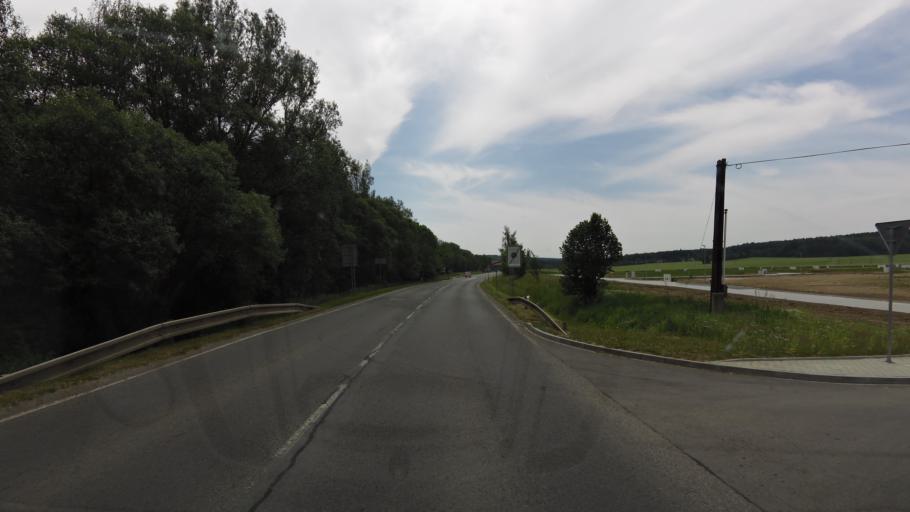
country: CZ
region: Plzensky
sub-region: Okres Rokycany
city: Rokycany
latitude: 49.7312
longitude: 13.5864
